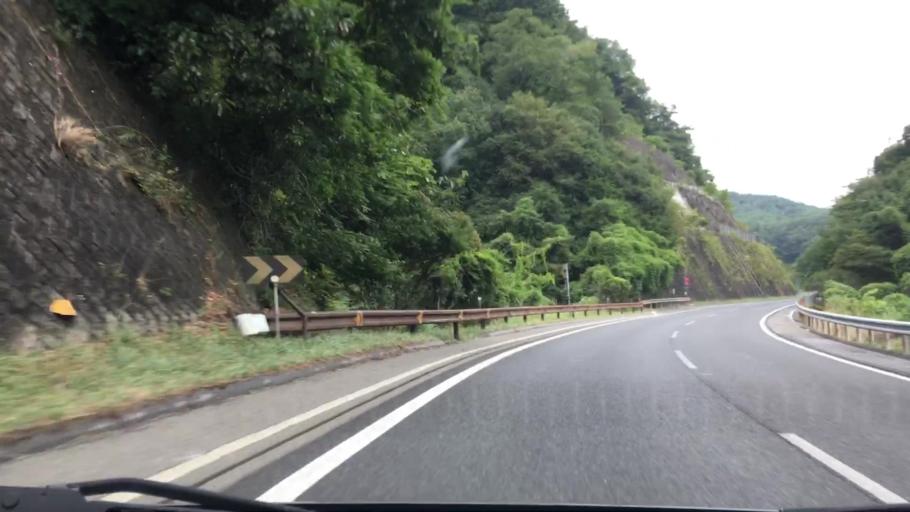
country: JP
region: Okayama
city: Niimi
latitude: 34.9885
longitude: 133.6059
